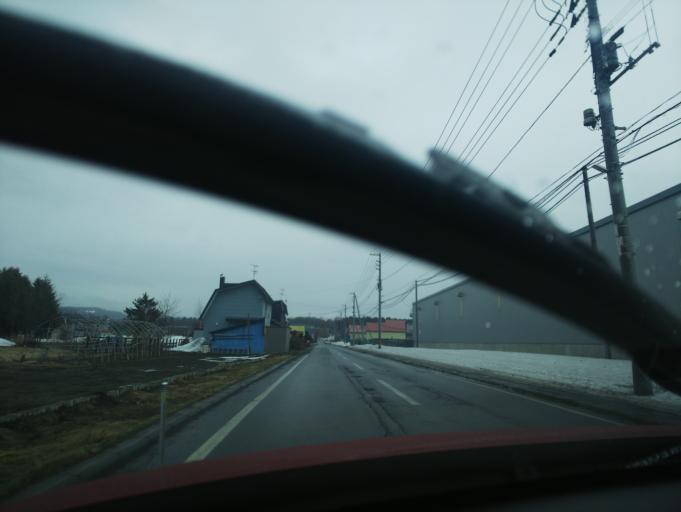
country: JP
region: Hokkaido
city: Nayoro
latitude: 44.3414
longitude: 142.4609
